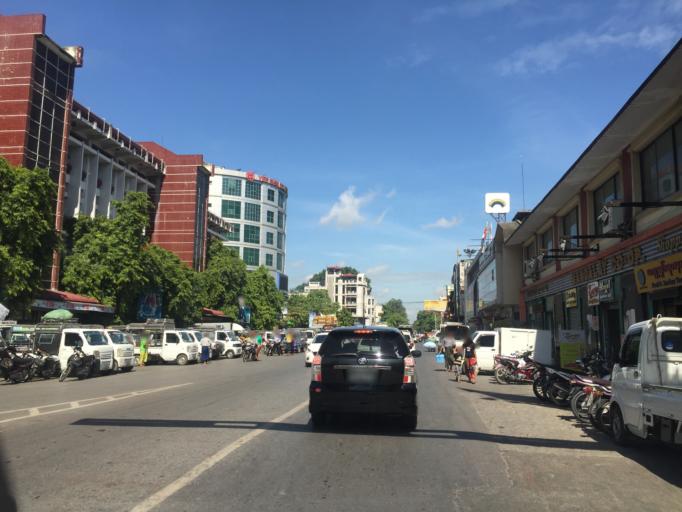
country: MM
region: Mandalay
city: Mandalay
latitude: 21.9836
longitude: 96.0777
